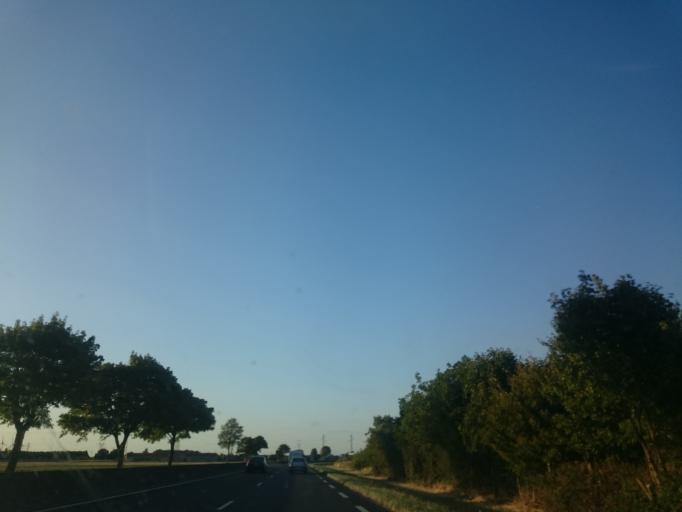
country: FR
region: Ile-de-France
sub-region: Departement de l'Essonne
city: Angerville
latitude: 48.3112
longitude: 1.9929
